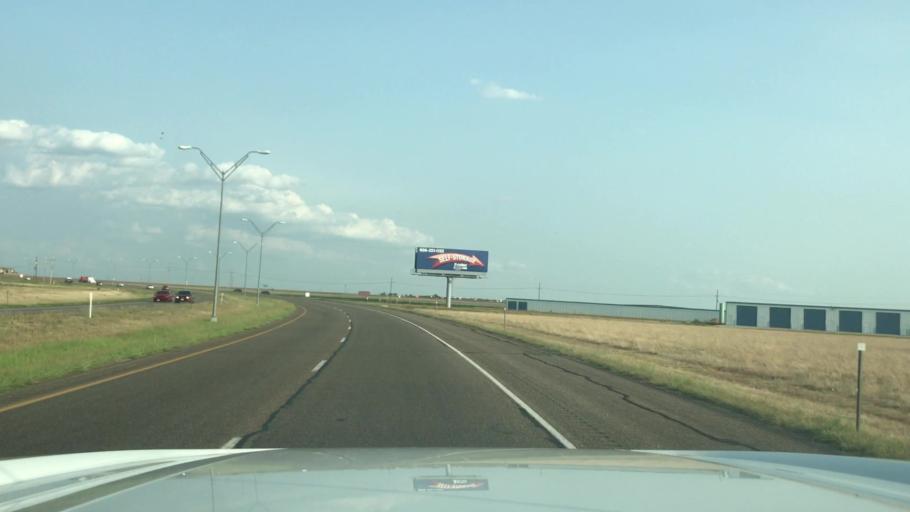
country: US
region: Texas
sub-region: Randall County
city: Canyon
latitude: 35.1200
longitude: -101.9368
